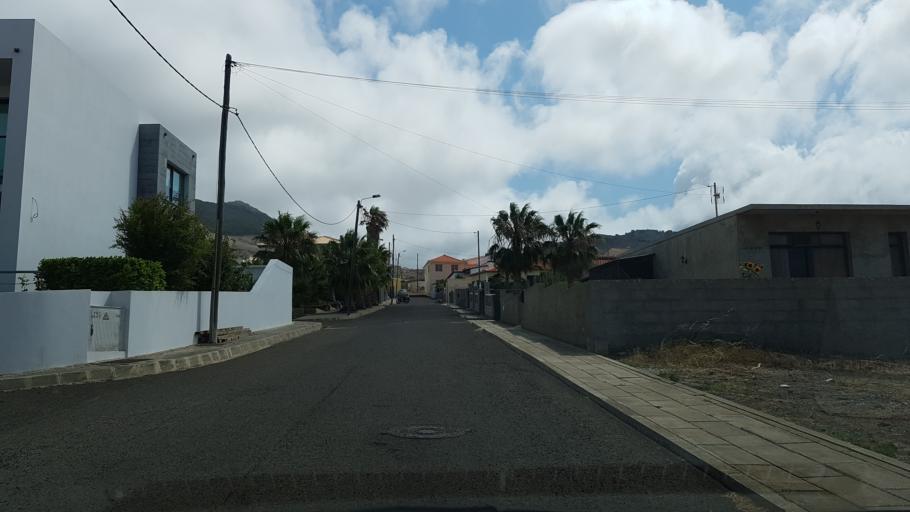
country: PT
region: Madeira
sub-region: Porto Santo
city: Vila de Porto Santo
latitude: 33.0682
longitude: -16.3347
